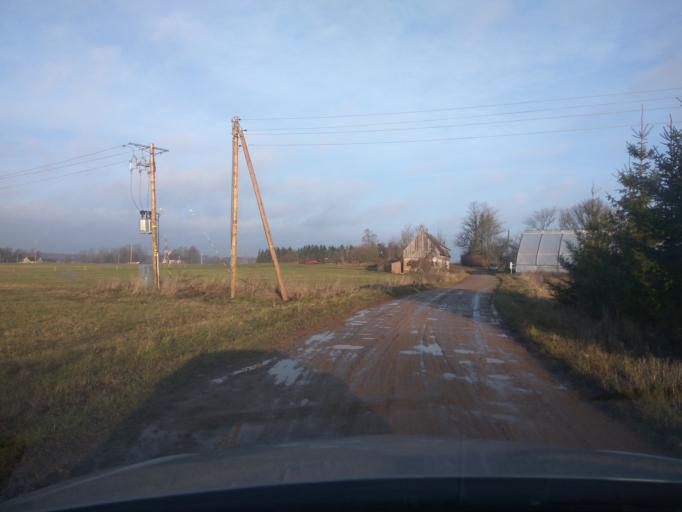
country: LV
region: Skrunda
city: Skrunda
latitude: 56.8438
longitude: 22.2213
